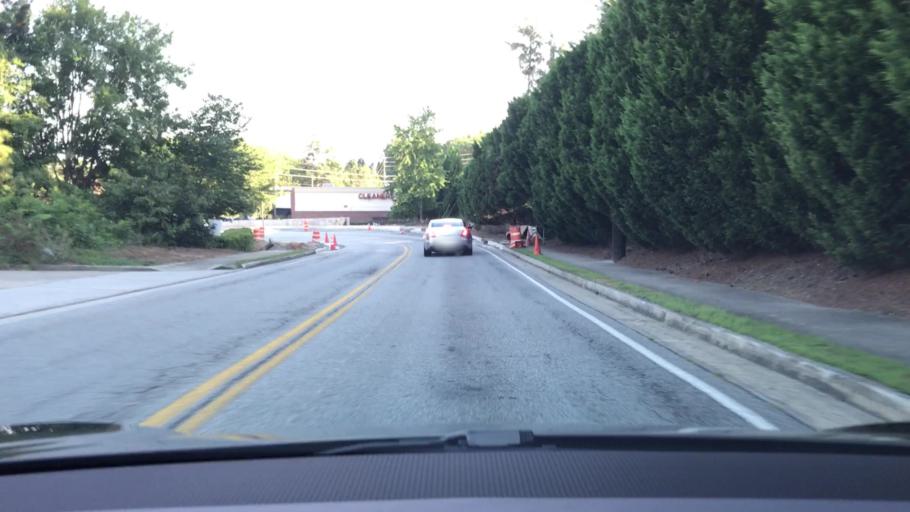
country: US
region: Georgia
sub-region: Fulton County
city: Johns Creek
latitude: 34.0626
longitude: -84.2262
